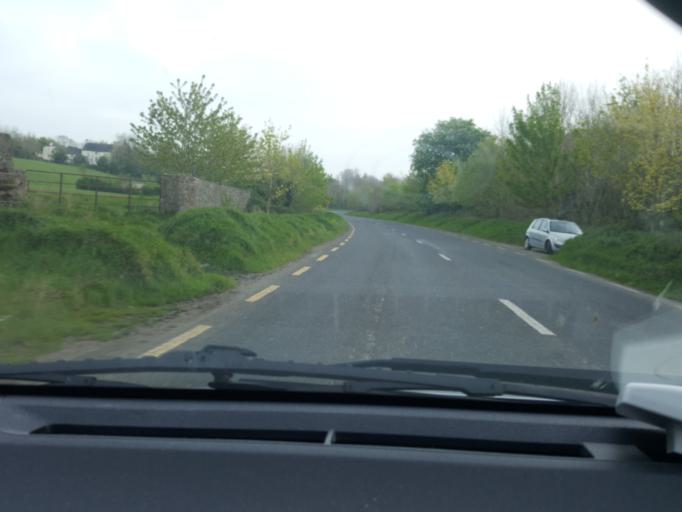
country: IE
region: Munster
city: Cahir
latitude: 52.3901
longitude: -7.9115
